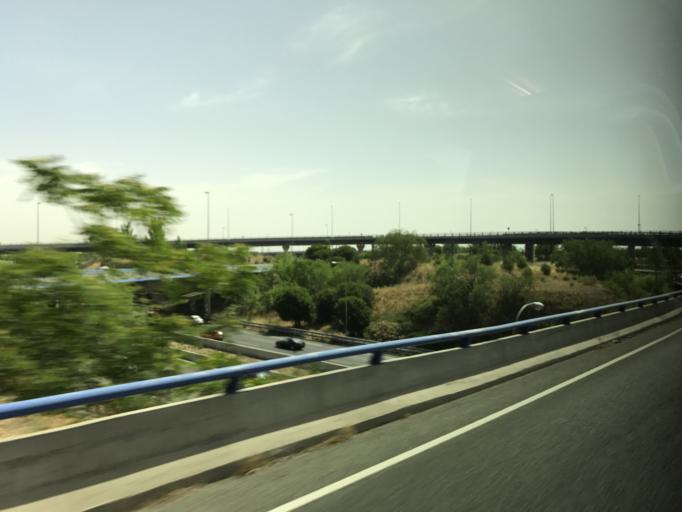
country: ES
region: Madrid
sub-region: Provincia de Madrid
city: Vicalvaro
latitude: 40.4125
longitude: -3.6215
